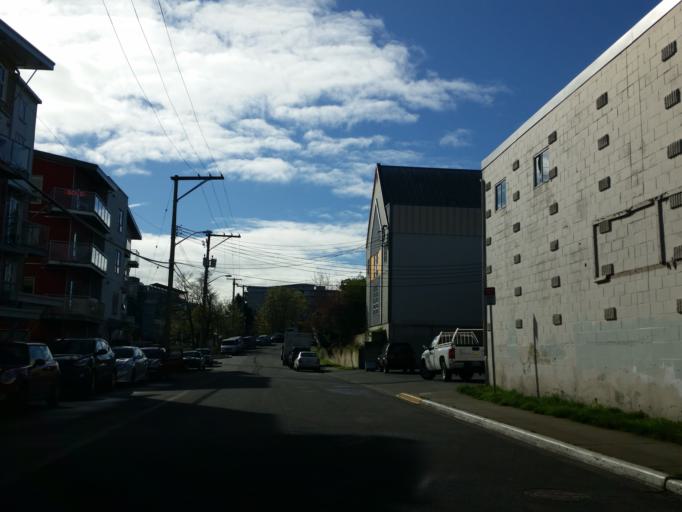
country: CA
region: British Columbia
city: Victoria
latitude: 48.4357
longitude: -123.3823
